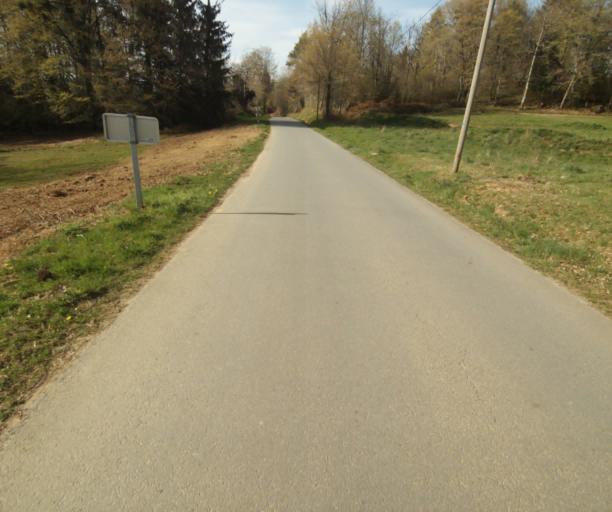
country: FR
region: Limousin
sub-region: Departement de la Correze
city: Naves
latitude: 45.3039
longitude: 1.7383
